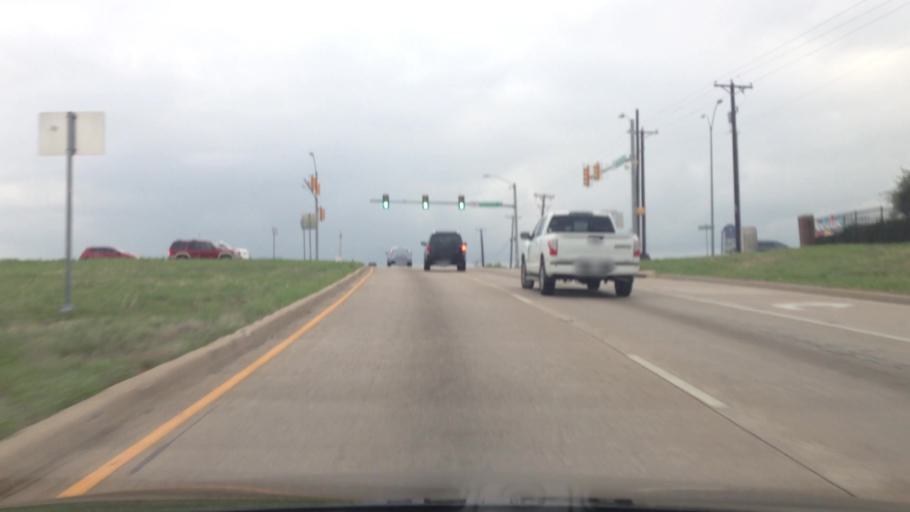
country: US
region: Texas
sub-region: Tarrant County
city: Crowley
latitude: 32.5780
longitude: -97.3279
